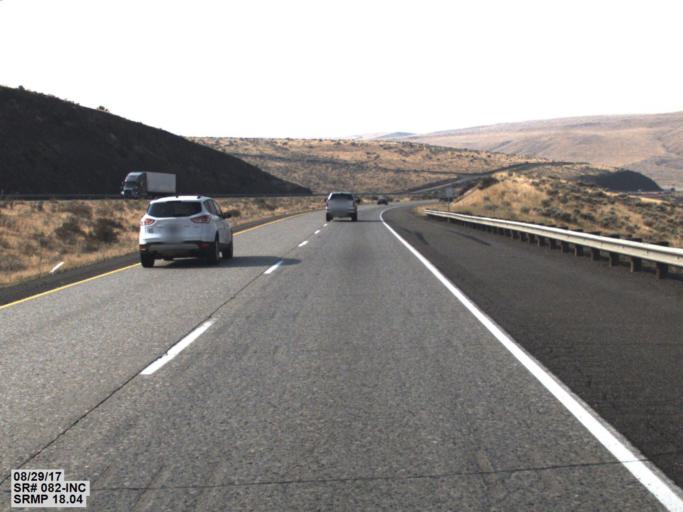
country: US
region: Washington
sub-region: Yakima County
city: Terrace Heights
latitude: 46.7616
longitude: -120.3797
